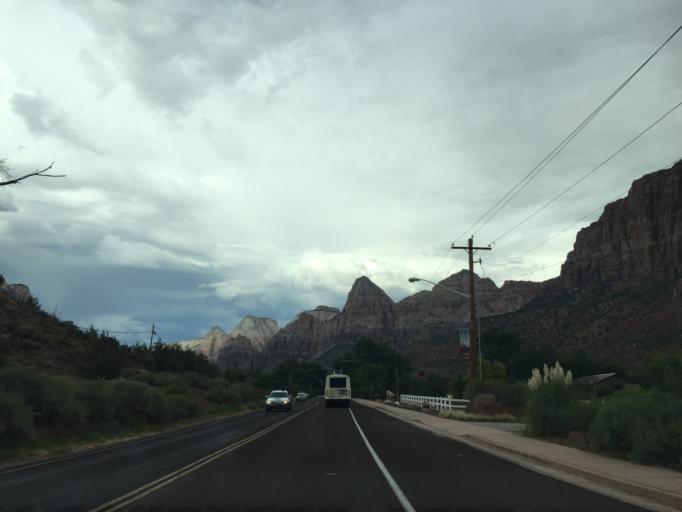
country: US
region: Utah
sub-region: Washington County
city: Hildale
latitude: 37.1819
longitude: -113.0053
